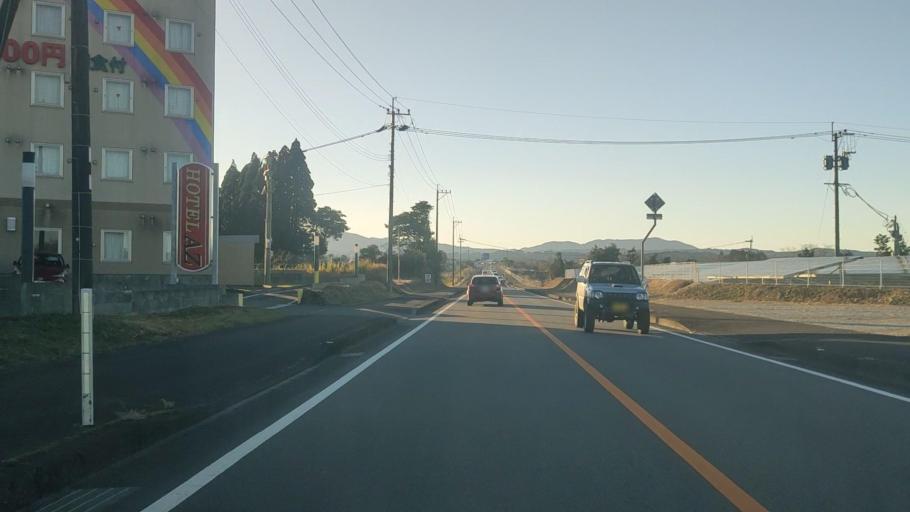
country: JP
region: Miyazaki
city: Miyazaki-shi
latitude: 31.8310
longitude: 131.3095
